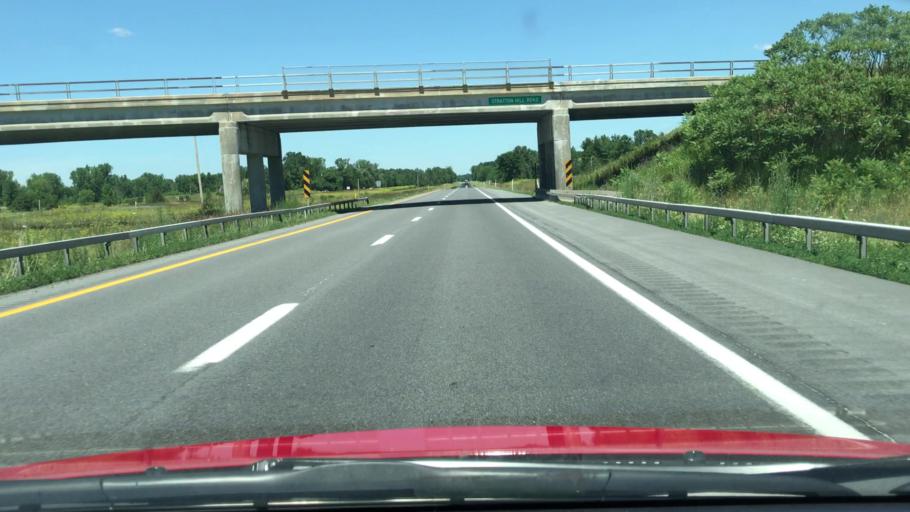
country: US
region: New York
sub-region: Clinton County
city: Cumberland Head
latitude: 44.8184
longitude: -73.4466
